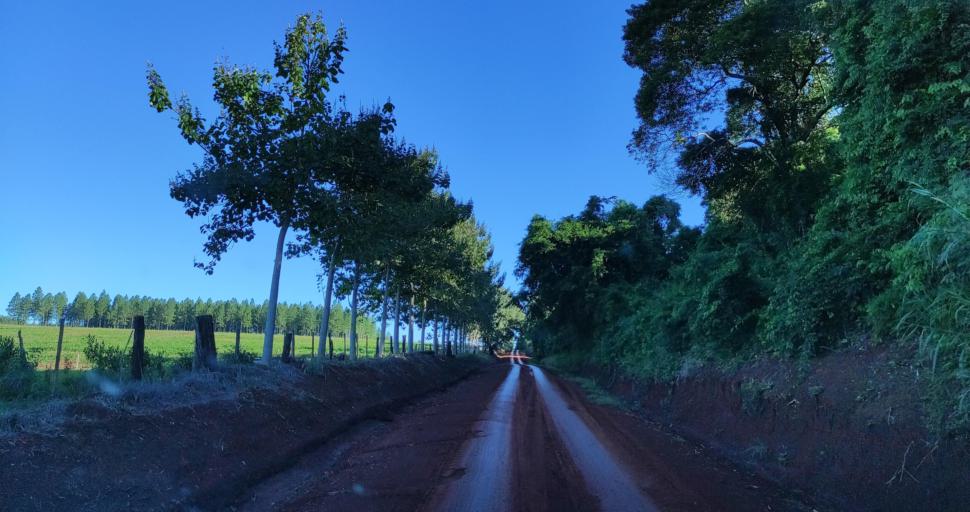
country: AR
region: Misiones
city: Puerto Rico
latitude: -26.8350
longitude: -55.0121
